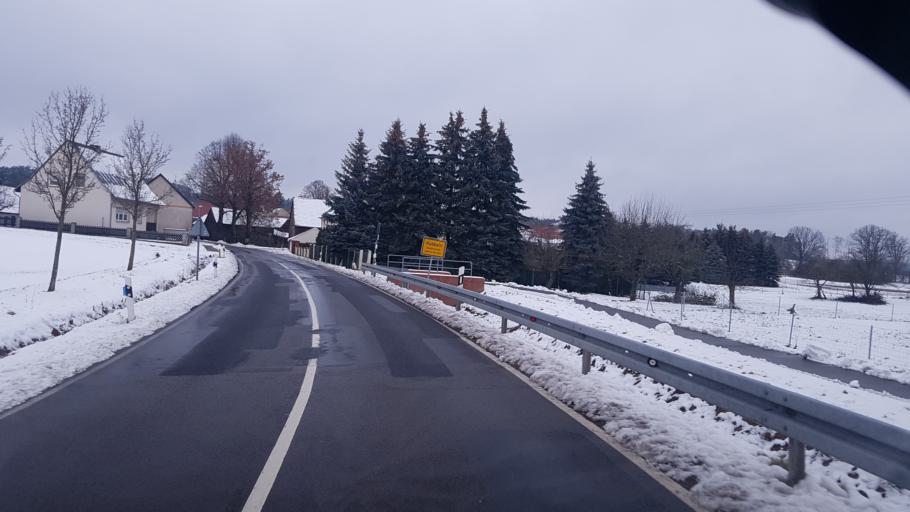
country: DE
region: Brandenburg
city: Lawitz
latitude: 52.0923
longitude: 14.5654
